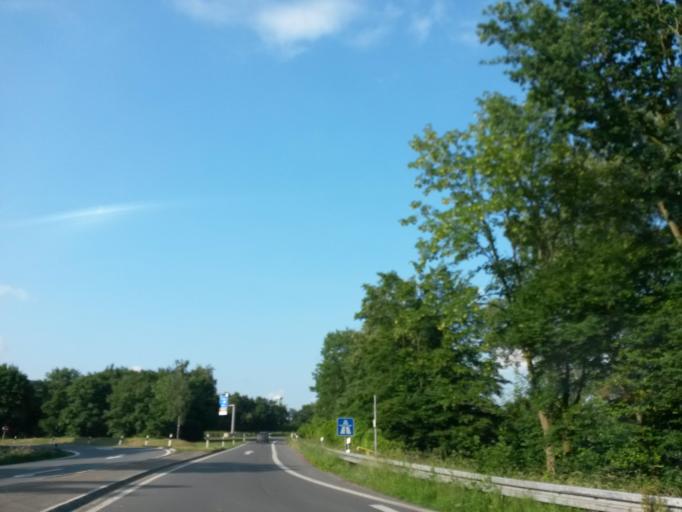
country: DE
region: North Rhine-Westphalia
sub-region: Regierungsbezirk Munster
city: Bottrop
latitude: 51.5379
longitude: 6.8726
